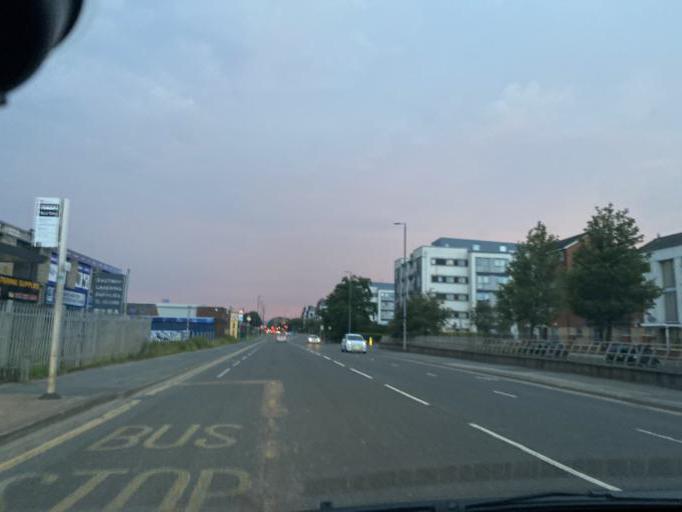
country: GB
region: England
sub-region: Manchester
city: Longsight
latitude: 53.4744
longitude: -2.1996
